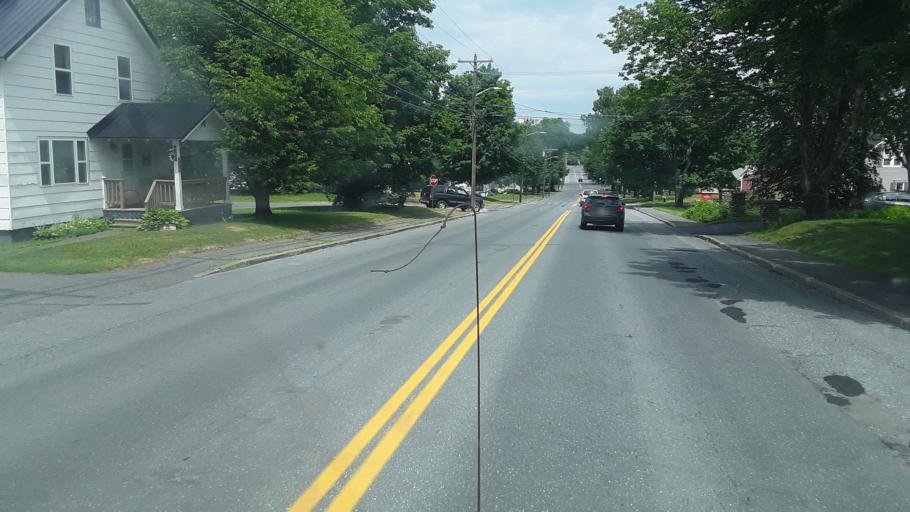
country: US
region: Maine
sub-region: Aroostook County
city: Fort Fairfield
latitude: 46.7691
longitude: -67.8423
